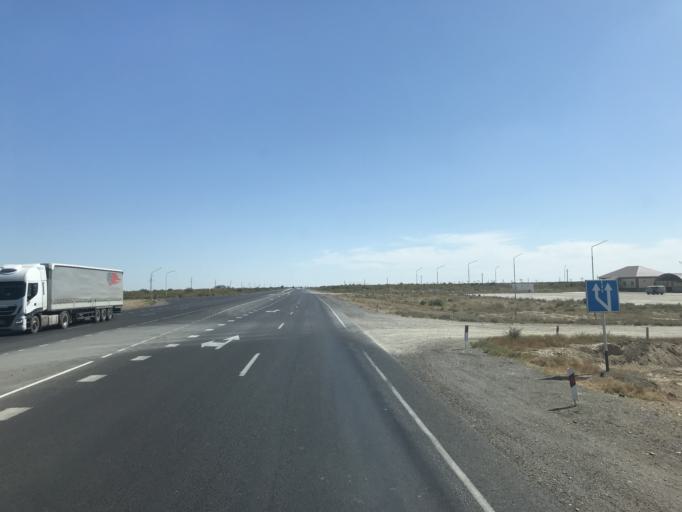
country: KZ
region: Qyzylorda
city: Belkol
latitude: 44.7657
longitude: 65.7785
